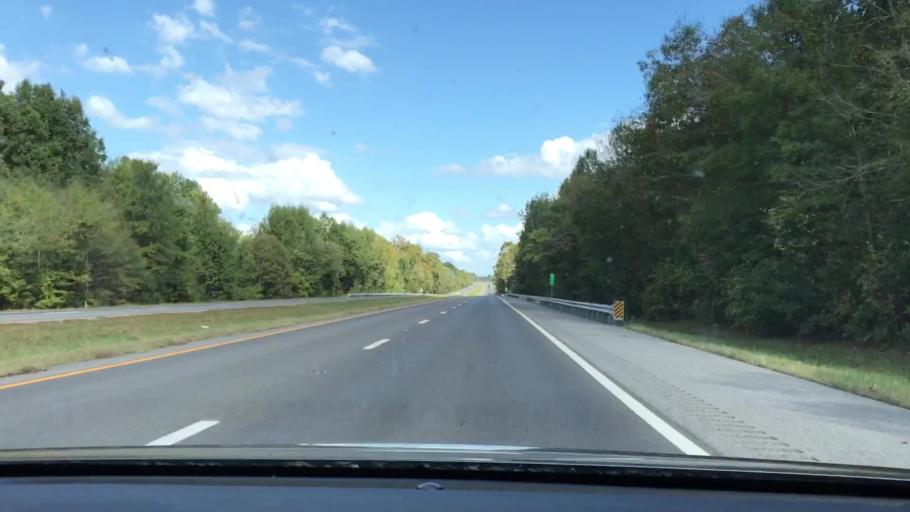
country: US
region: Kentucky
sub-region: Marshall County
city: Benton
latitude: 36.8316
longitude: -88.4448
